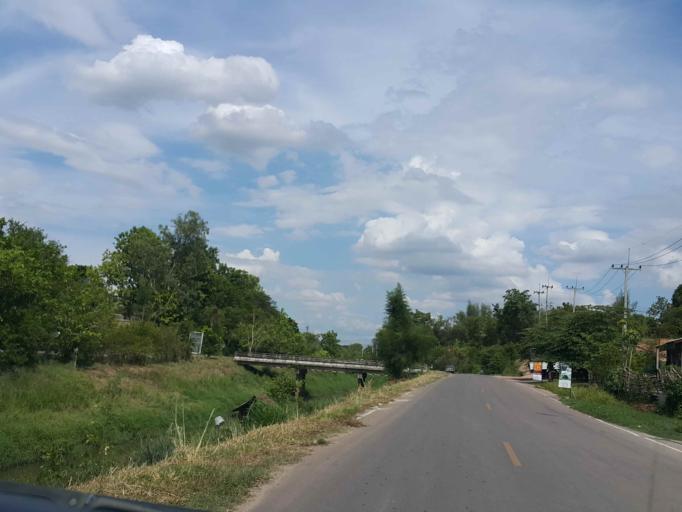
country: TH
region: Chiang Mai
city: San Sai
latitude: 18.9230
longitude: 98.9360
